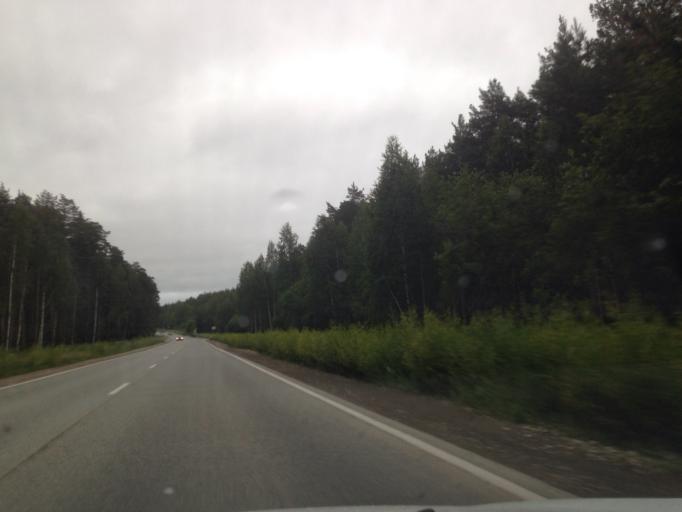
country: RU
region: Sverdlovsk
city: Istok
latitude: 56.8402
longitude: 60.7577
